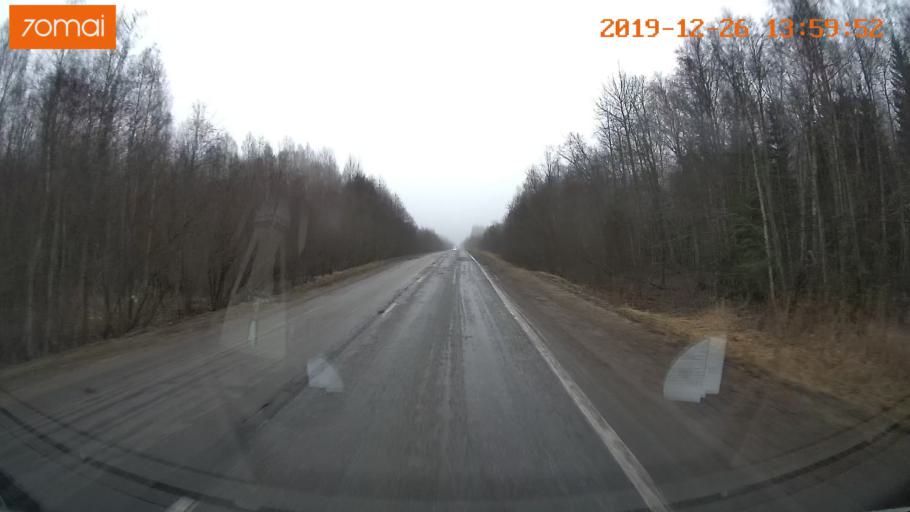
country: RU
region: Jaroslavl
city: Poshekhon'ye
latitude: 58.5622
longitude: 38.7324
